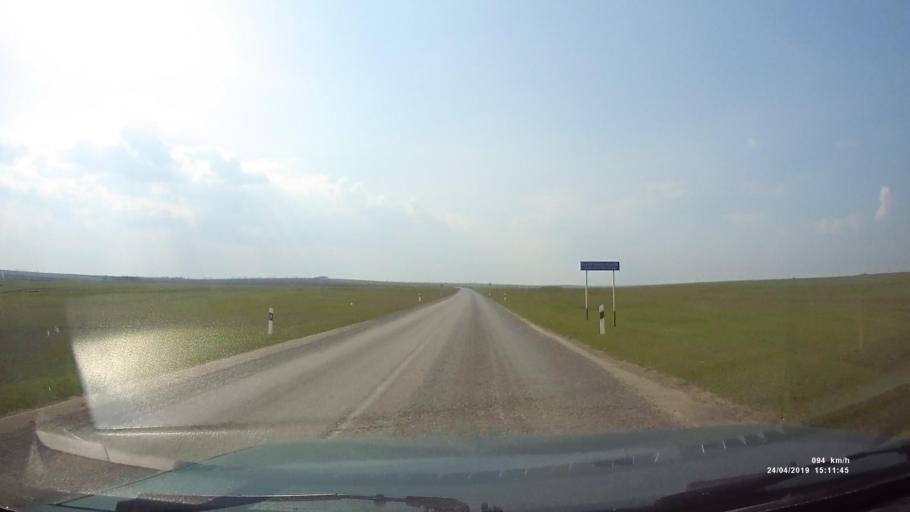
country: RU
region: Rostov
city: Remontnoye
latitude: 46.5443
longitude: 43.3152
